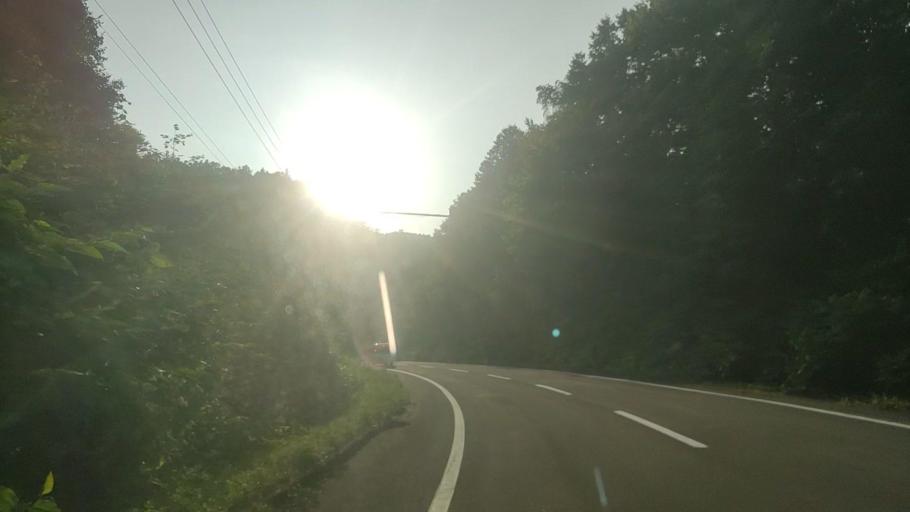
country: JP
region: Hokkaido
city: Bibai
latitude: 43.1779
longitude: 142.0687
